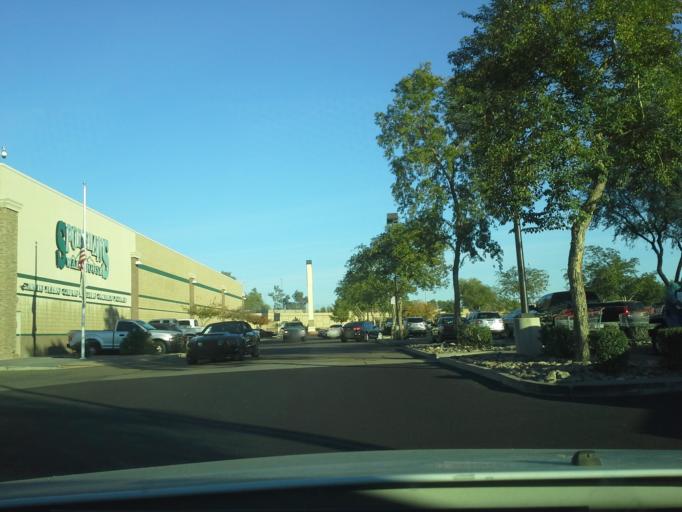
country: US
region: Arizona
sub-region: Maricopa County
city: Glendale
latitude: 33.6609
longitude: -112.1162
